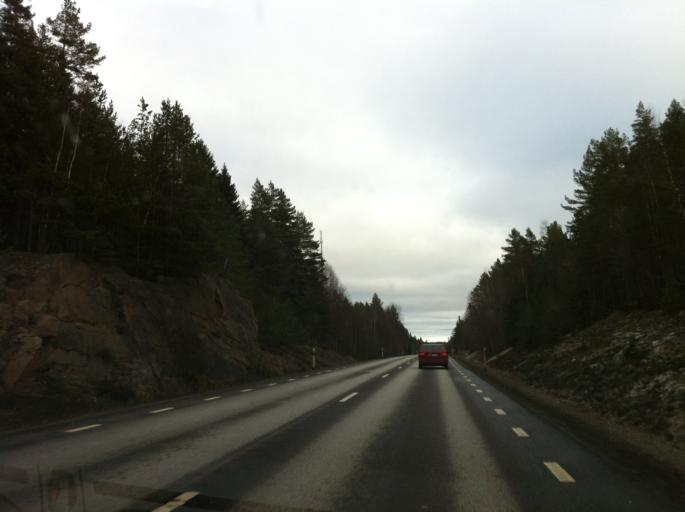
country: SE
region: Kalmar
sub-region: Vimmerby Kommun
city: Vimmerby
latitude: 57.6399
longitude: 15.7643
